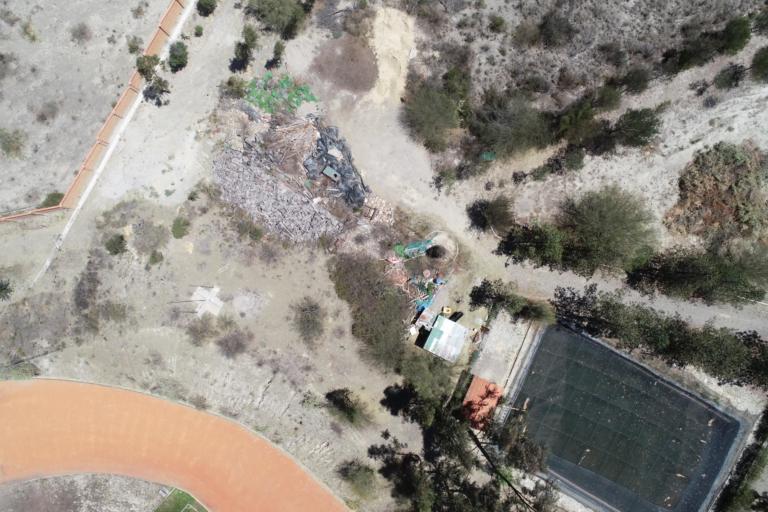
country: BO
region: La Paz
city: La Paz
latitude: -16.6276
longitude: -68.0586
